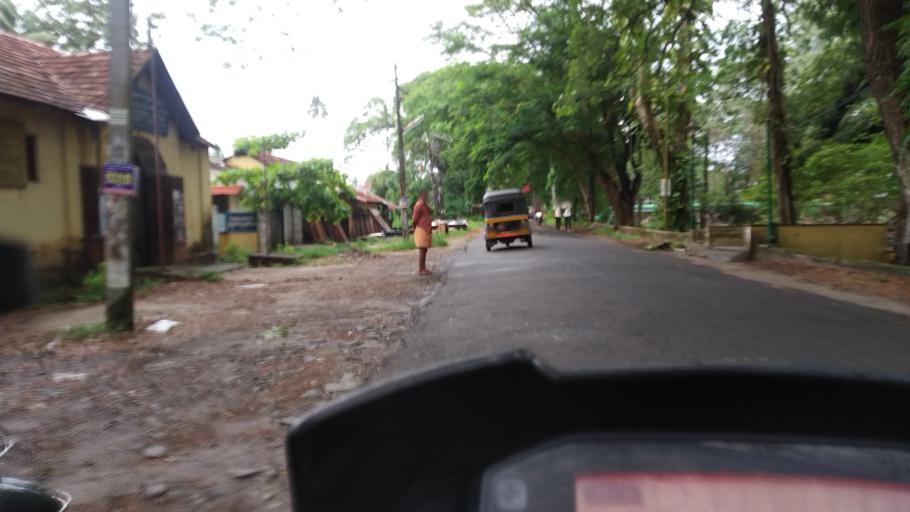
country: IN
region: Kerala
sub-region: Alappuzha
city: Alleppey
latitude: 9.5002
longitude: 76.3245
